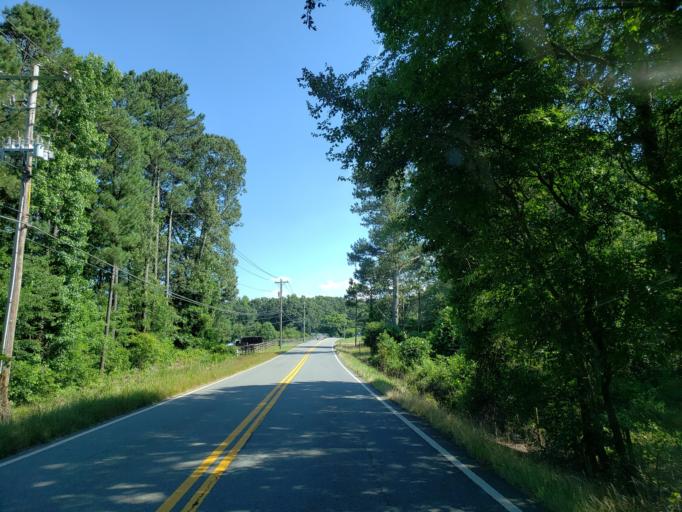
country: US
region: Georgia
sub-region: Cherokee County
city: Holly Springs
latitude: 34.1179
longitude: -84.4237
